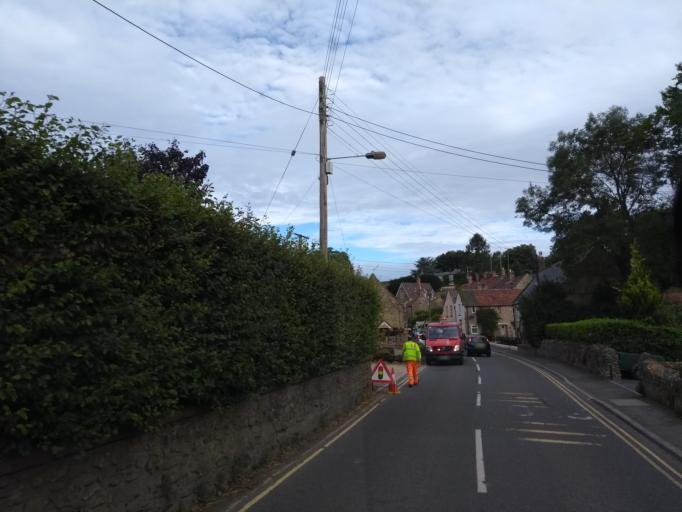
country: GB
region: England
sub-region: Somerset
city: Crewkerne
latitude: 50.8702
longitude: -2.7748
